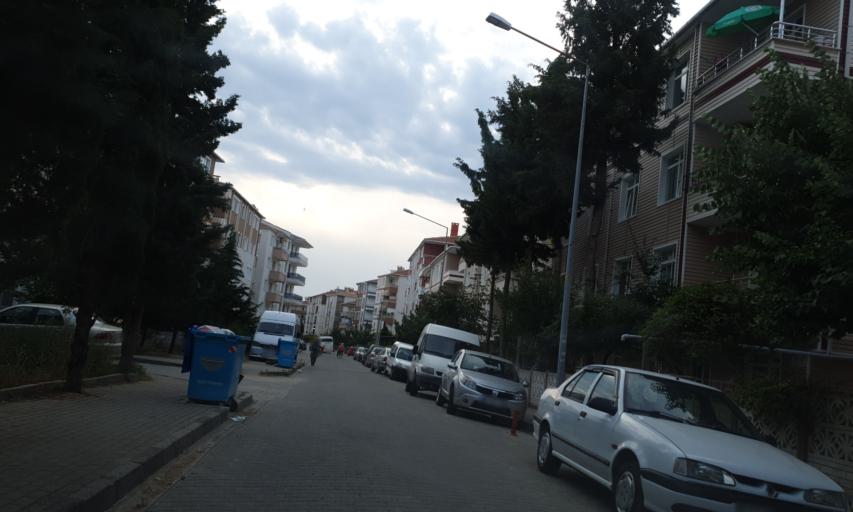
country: TR
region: Kirklareli
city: Luleburgaz
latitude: 41.4045
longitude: 27.3655
